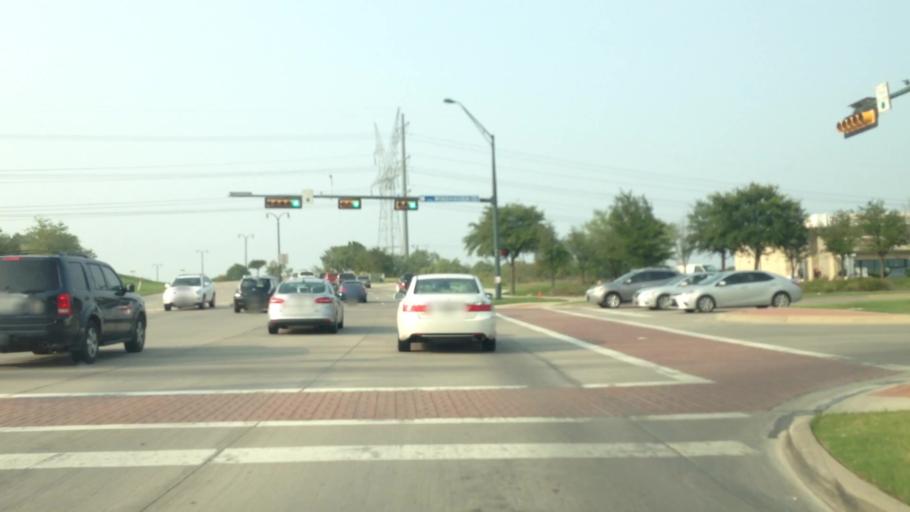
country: US
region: Texas
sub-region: Denton County
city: The Colony
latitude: 33.0582
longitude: -96.8631
